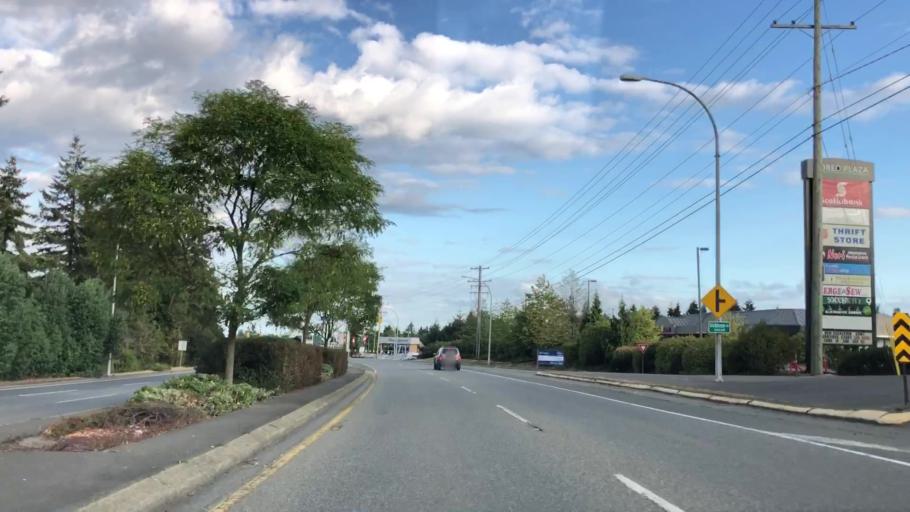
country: CA
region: British Columbia
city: Nanaimo
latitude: 49.2369
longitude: -124.0465
